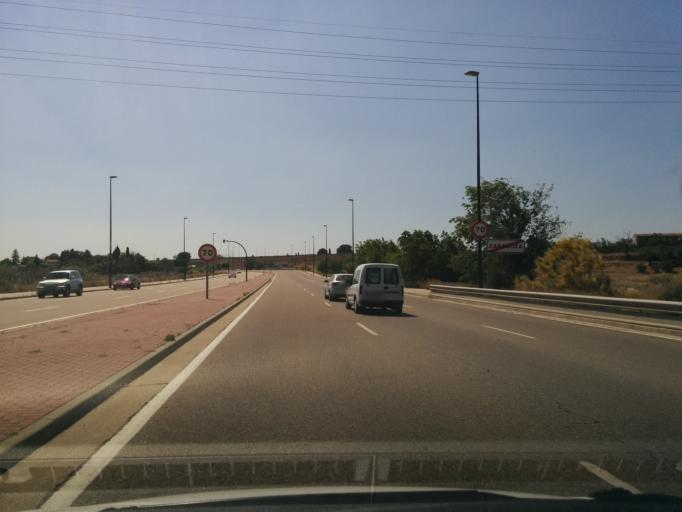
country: ES
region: Aragon
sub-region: Provincia de Zaragoza
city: Zaragoza
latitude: 41.6240
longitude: -0.8671
